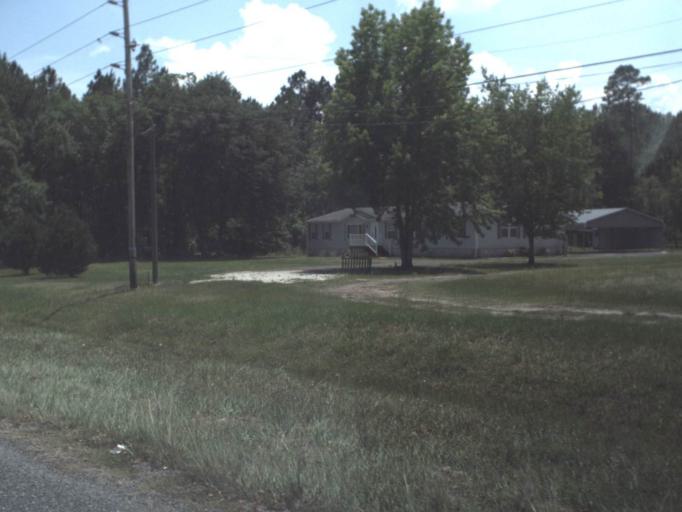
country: US
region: Florida
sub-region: Clay County
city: Green Cove Springs
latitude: 29.8232
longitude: -81.6608
